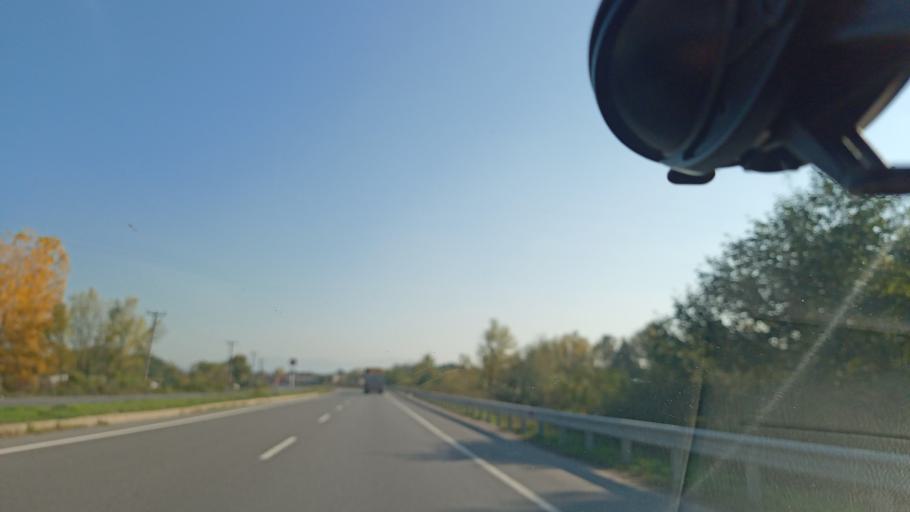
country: TR
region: Sakarya
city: Karasu
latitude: 41.0709
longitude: 30.7942
